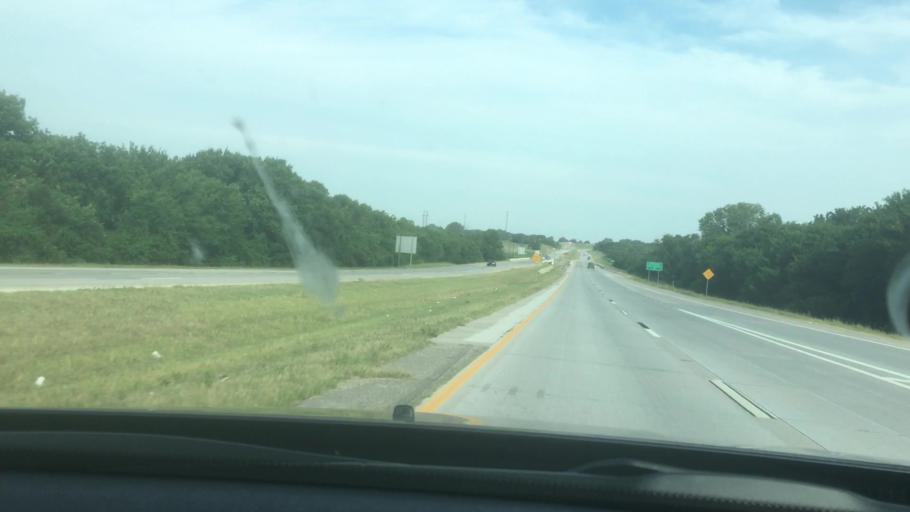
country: US
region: Oklahoma
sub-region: Pontotoc County
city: Ada
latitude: 34.7778
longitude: -96.7059
